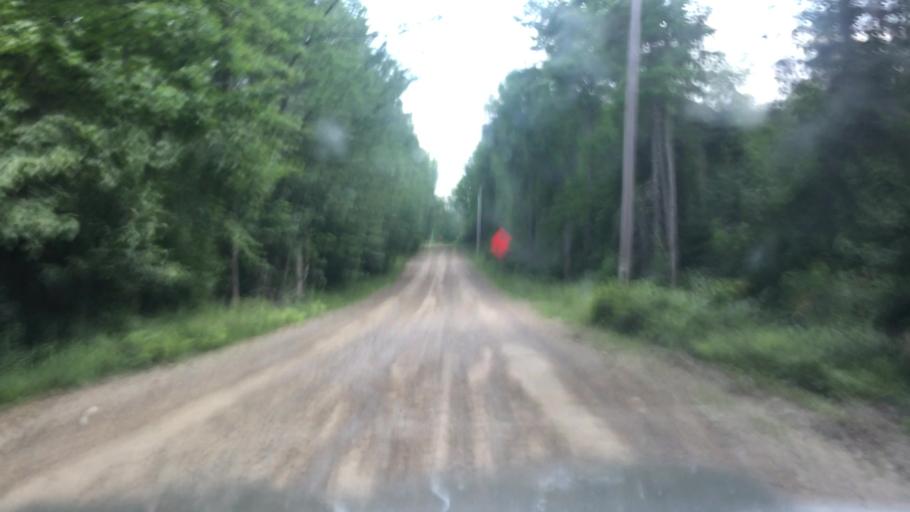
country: US
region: Maine
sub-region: Waldo County
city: Searsmont
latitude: 44.4043
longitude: -69.2748
